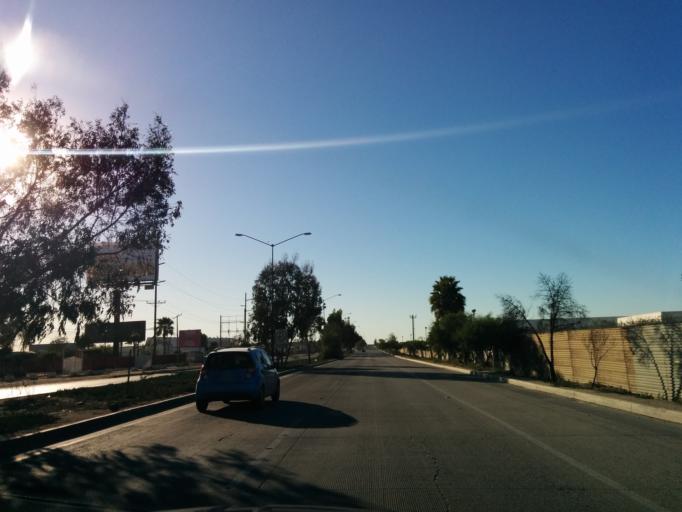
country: MX
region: Baja California
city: Tijuana
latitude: 32.5489
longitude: -116.9526
